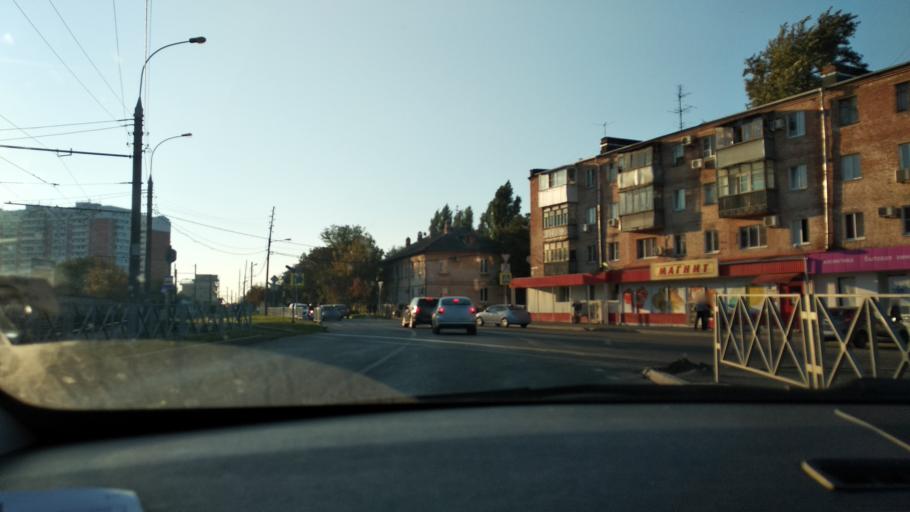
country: RU
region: Krasnodarskiy
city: Krasnodar
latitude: 45.0068
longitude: 39.0165
